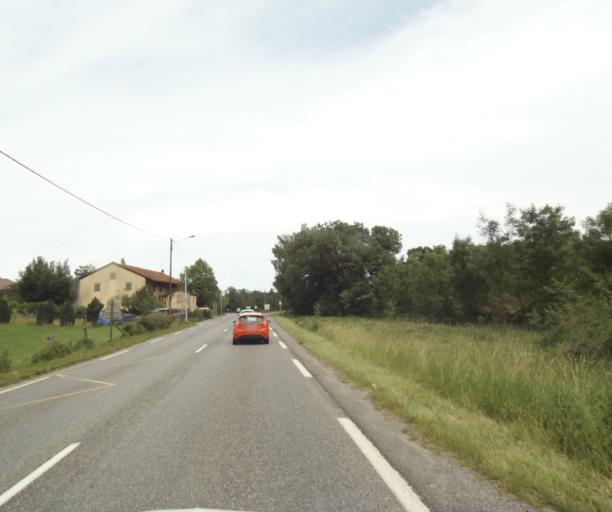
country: FR
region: Rhone-Alpes
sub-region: Departement de la Haute-Savoie
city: Allinges
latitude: 46.3476
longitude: 6.4655
